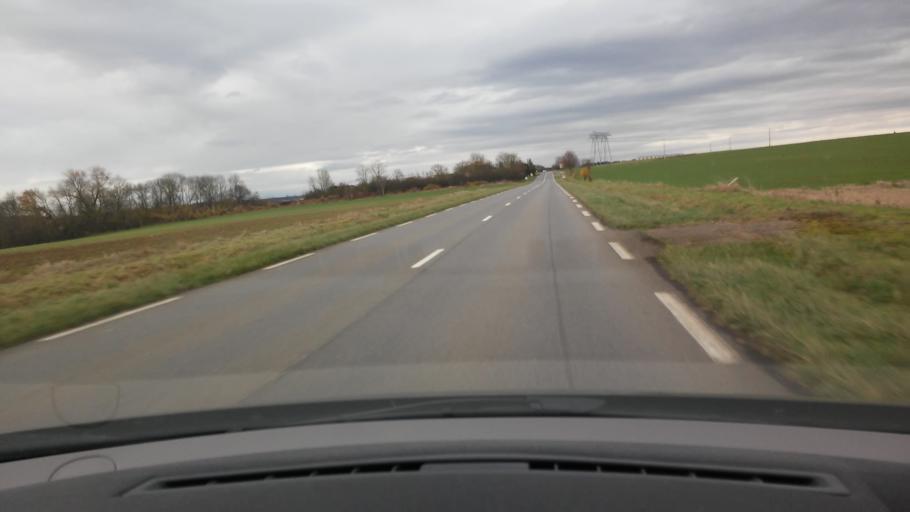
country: FR
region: Lorraine
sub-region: Departement de la Moselle
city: Retonfey
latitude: 49.1576
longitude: 6.2757
